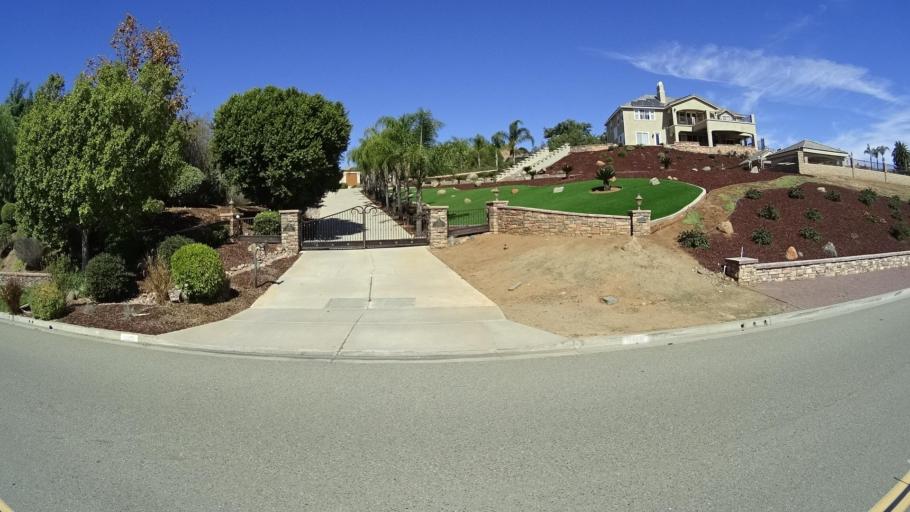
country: US
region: California
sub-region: San Diego County
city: Harbison Canyon
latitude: 32.8768
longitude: -116.8403
